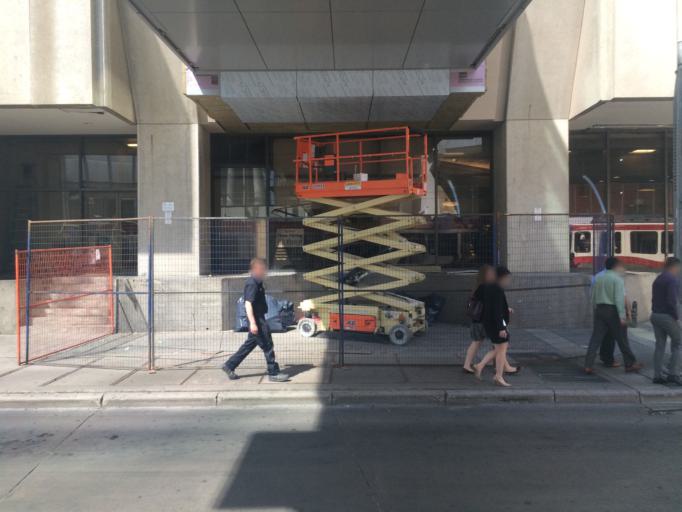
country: CA
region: Alberta
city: Calgary
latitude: 51.0466
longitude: -114.0667
